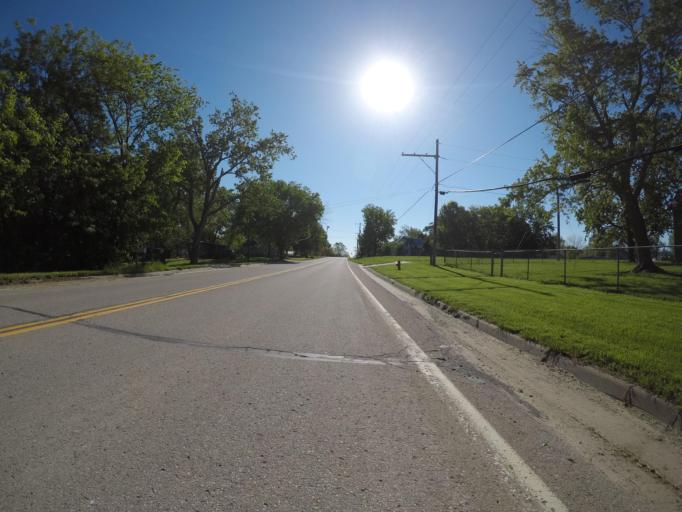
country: US
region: Kansas
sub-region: Douglas County
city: Lawrence
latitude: 39.0439
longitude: -95.3986
